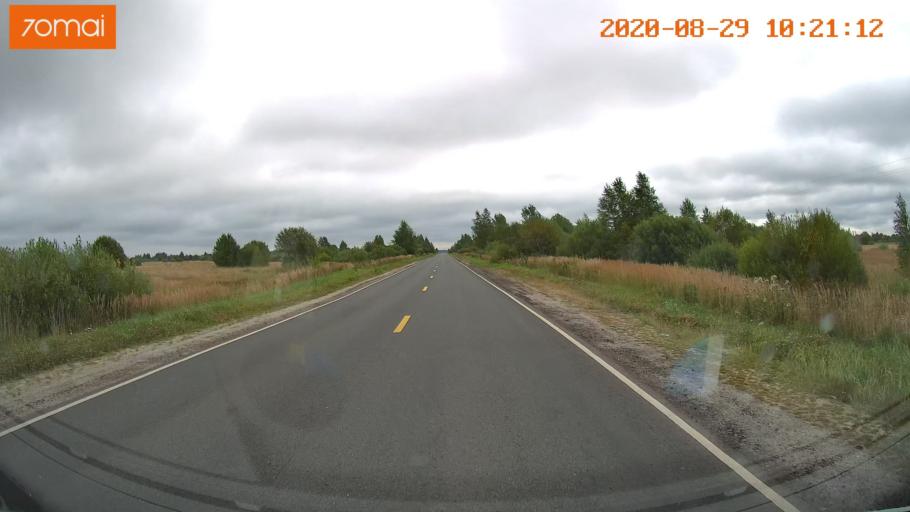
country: RU
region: Ivanovo
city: Yur'yevets
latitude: 57.3229
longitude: 42.9125
